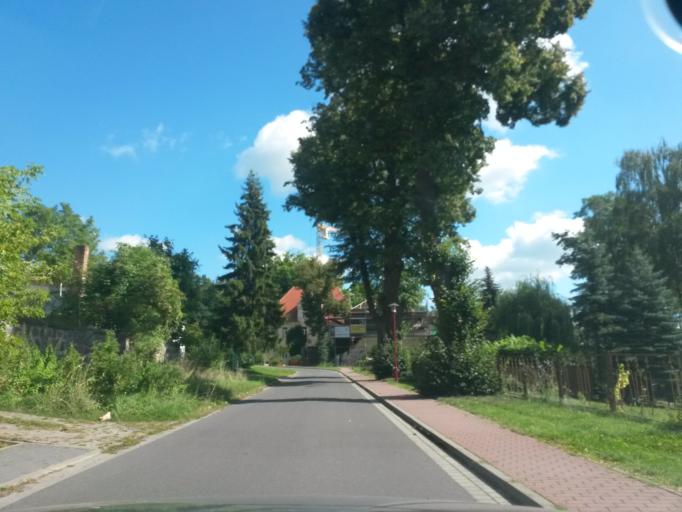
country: DE
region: Brandenburg
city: Schoneberg
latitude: 52.9797
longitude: 14.1173
